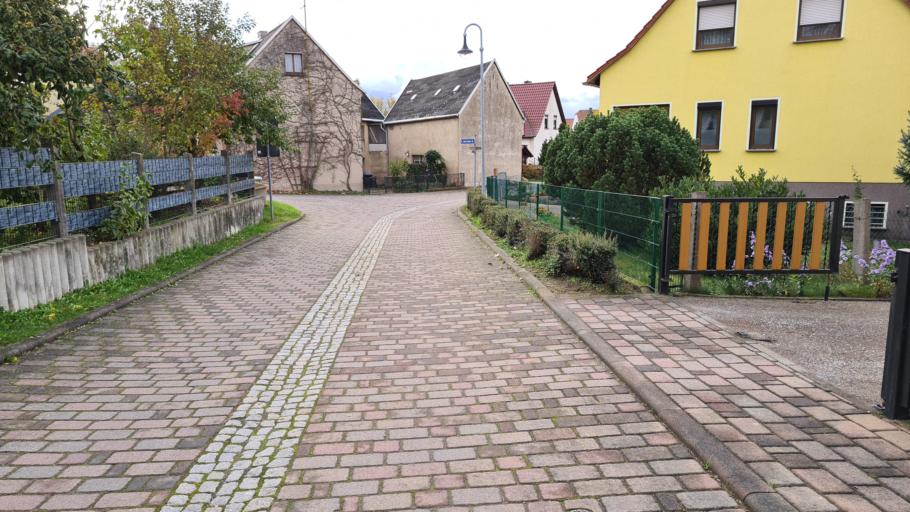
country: DE
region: Saxony
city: Dahlen
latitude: 51.3999
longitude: 12.9877
